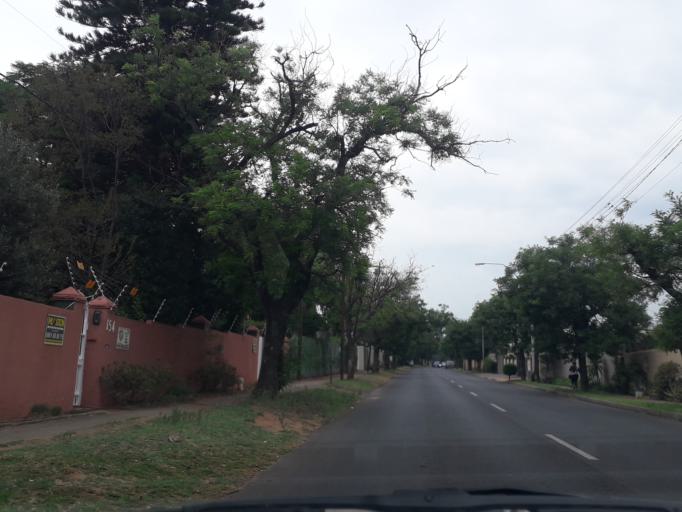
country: ZA
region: Gauteng
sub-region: City of Johannesburg Metropolitan Municipality
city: Johannesburg
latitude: -26.1423
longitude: 28.0930
